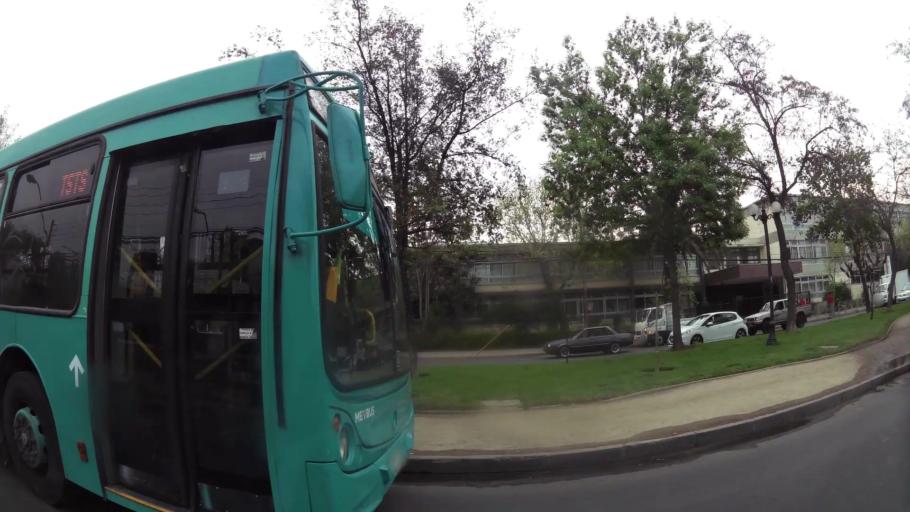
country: CL
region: Santiago Metropolitan
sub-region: Provincia de Santiago
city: Santiago
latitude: -33.4467
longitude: -70.6305
